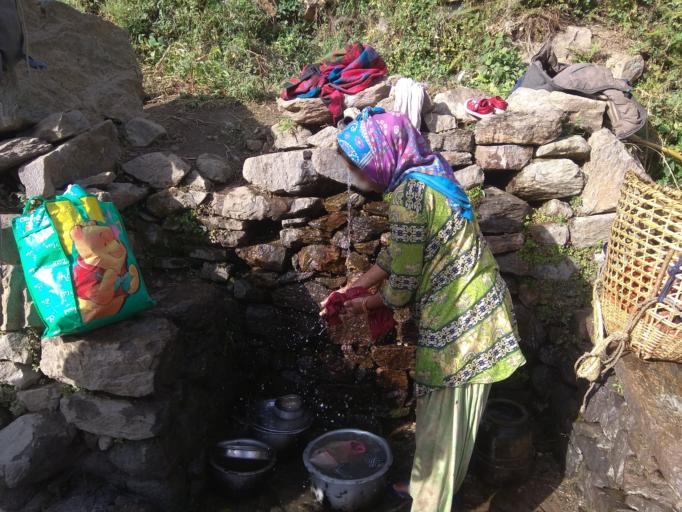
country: NP
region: Mid Western
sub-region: Bheri Zone
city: Dailekh
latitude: 29.2349
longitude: 81.6497
